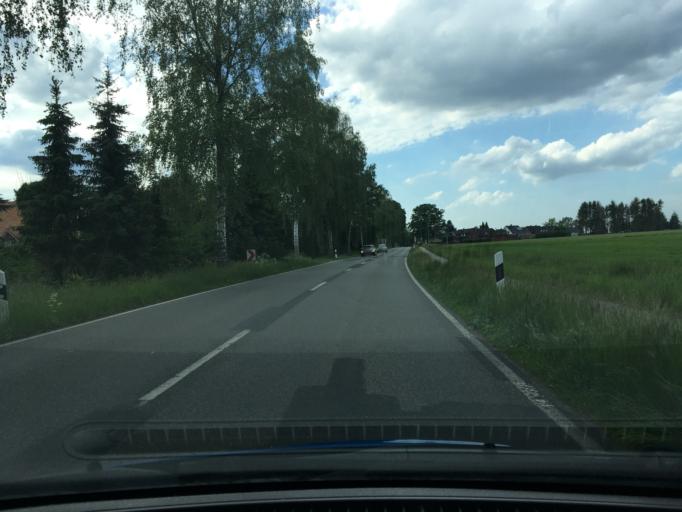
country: DE
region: Lower Saxony
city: Otter
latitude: 53.2580
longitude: 9.7427
